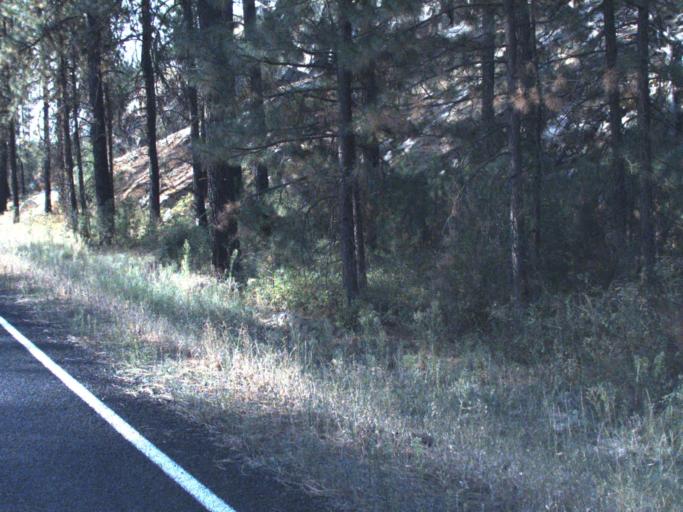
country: US
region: Washington
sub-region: Spokane County
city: Airway Heights
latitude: 47.8599
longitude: -117.7121
